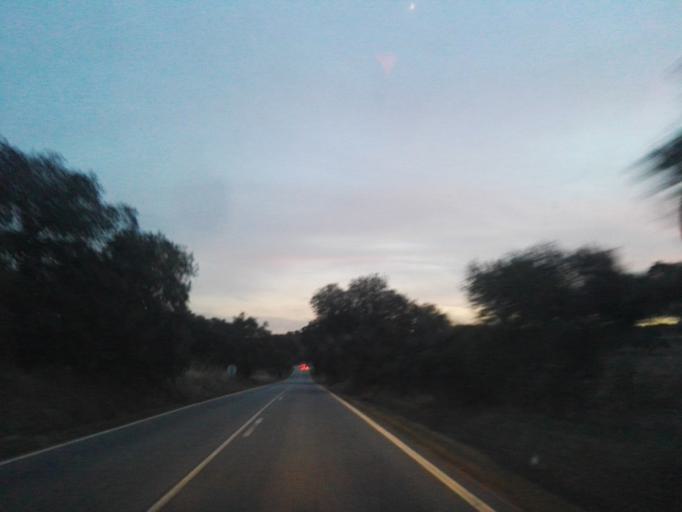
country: PT
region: Portalegre
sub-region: Elvas
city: Elvas
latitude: 38.9155
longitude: -7.1822
